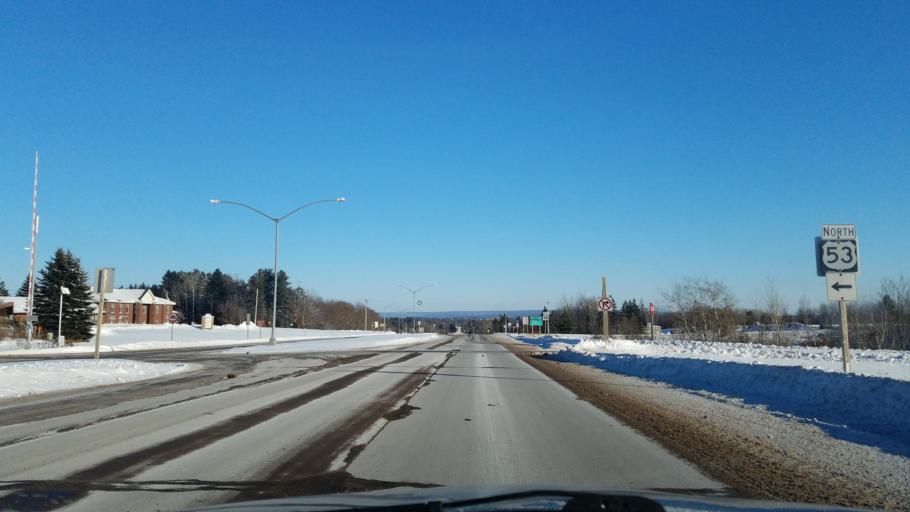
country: US
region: Wisconsin
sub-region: Barron County
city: Rice Lake
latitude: 45.5092
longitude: -91.7612
